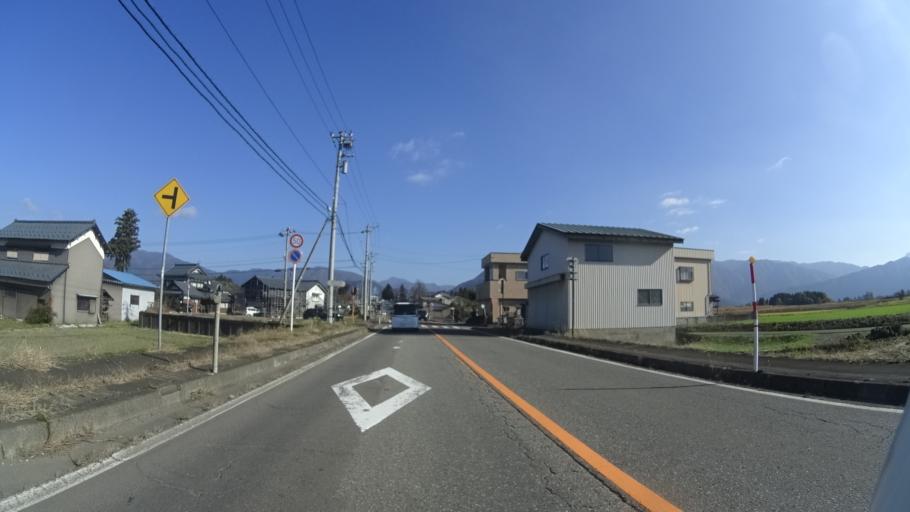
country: JP
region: Fukui
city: Ono
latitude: 35.9799
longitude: 136.5255
